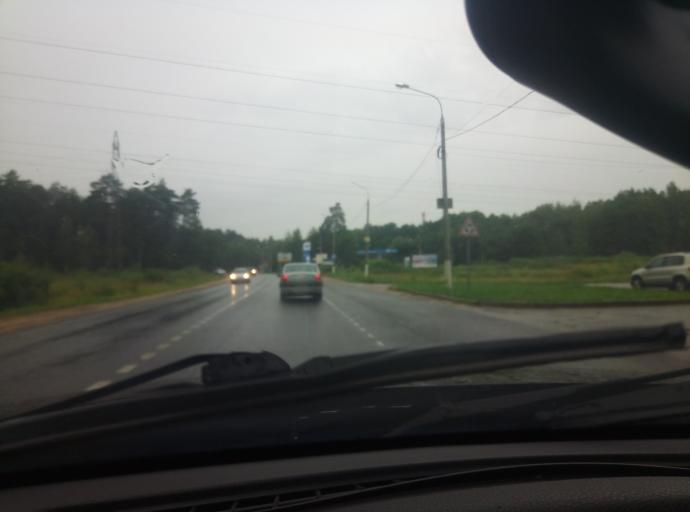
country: RU
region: Moskovskaya
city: Protvino
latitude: 54.8791
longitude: 37.2403
